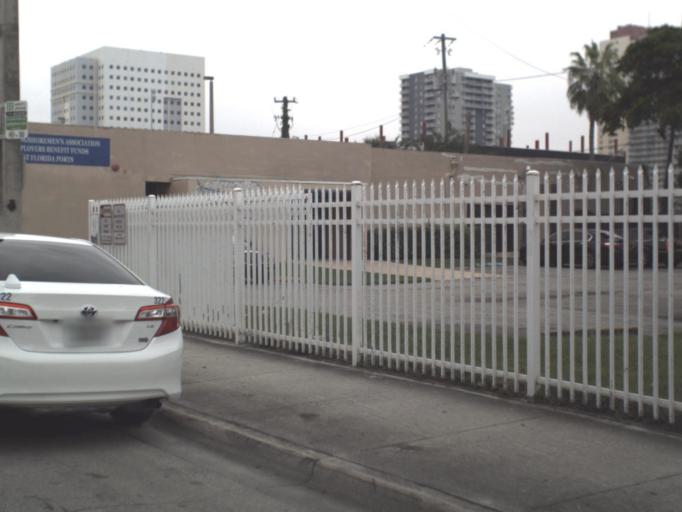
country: US
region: Florida
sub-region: Miami-Dade County
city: Miami
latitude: 25.7800
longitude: -80.1927
